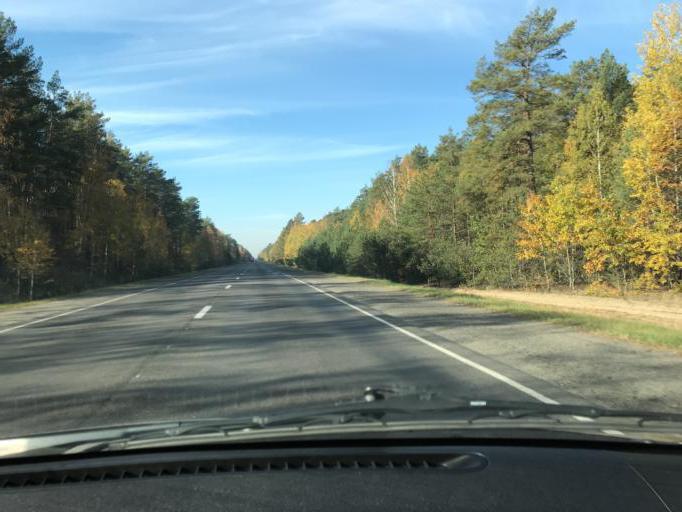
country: BY
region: Brest
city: Mikashevichy
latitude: 52.2416
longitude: 27.3204
